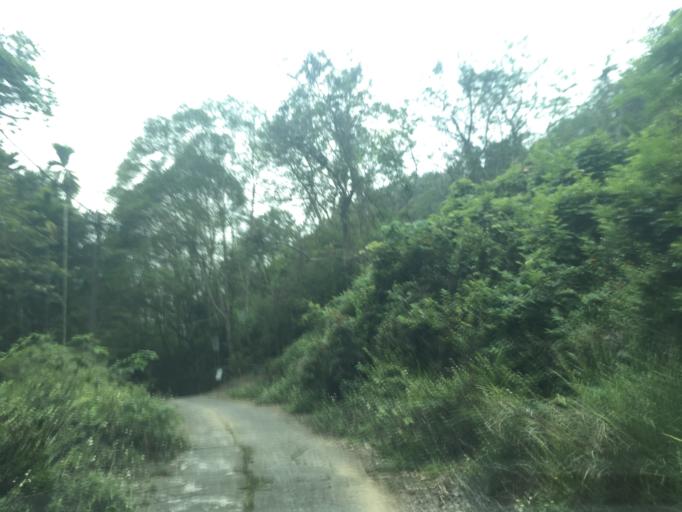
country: TW
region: Taiwan
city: Zhongxing New Village
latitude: 24.0466
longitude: 120.8055
